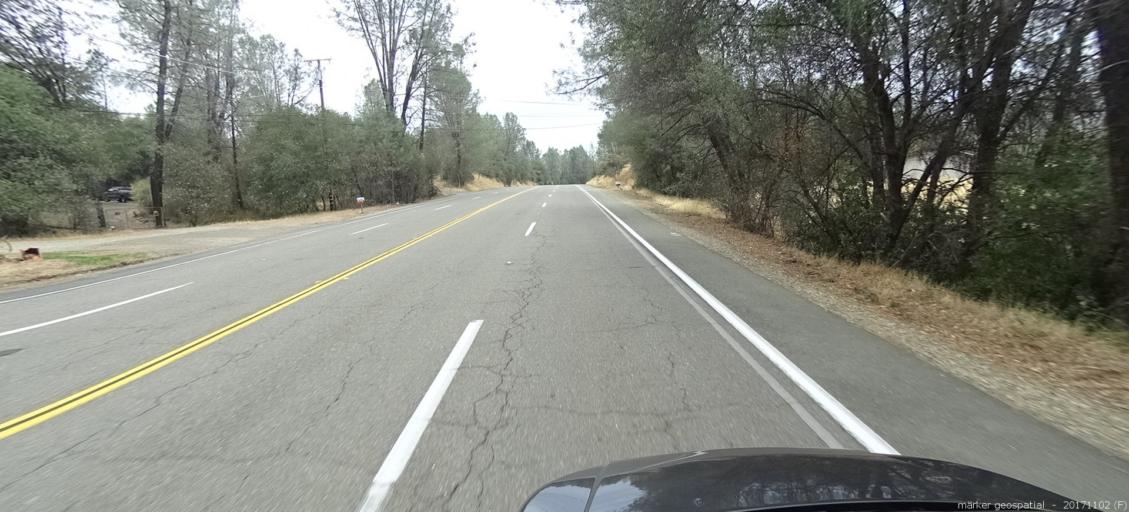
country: US
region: California
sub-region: Shasta County
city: Central Valley (historical)
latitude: 40.6577
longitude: -122.3966
